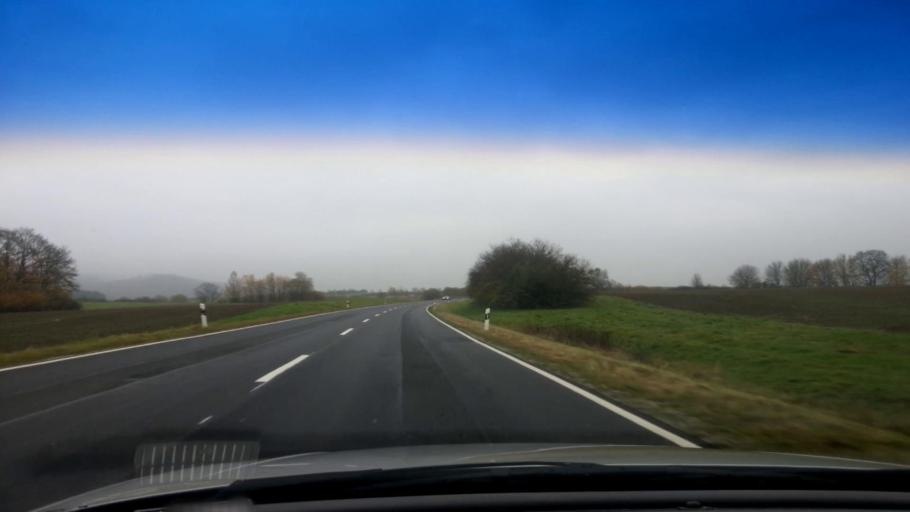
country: DE
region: Bavaria
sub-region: Upper Franconia
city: Litzendorf
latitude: 49.8852
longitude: 10.9895
